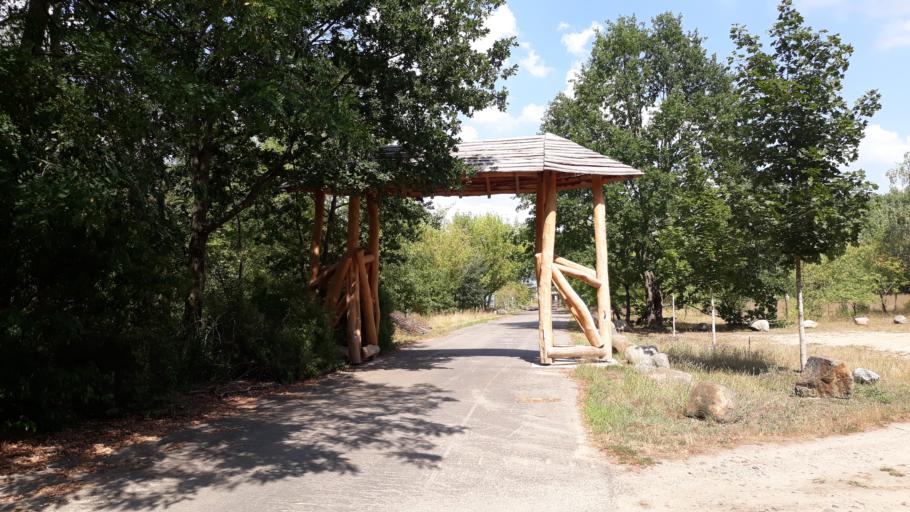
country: DE
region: Brandenburg
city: Heinersbruck
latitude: 51.7457
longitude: 14.5184
